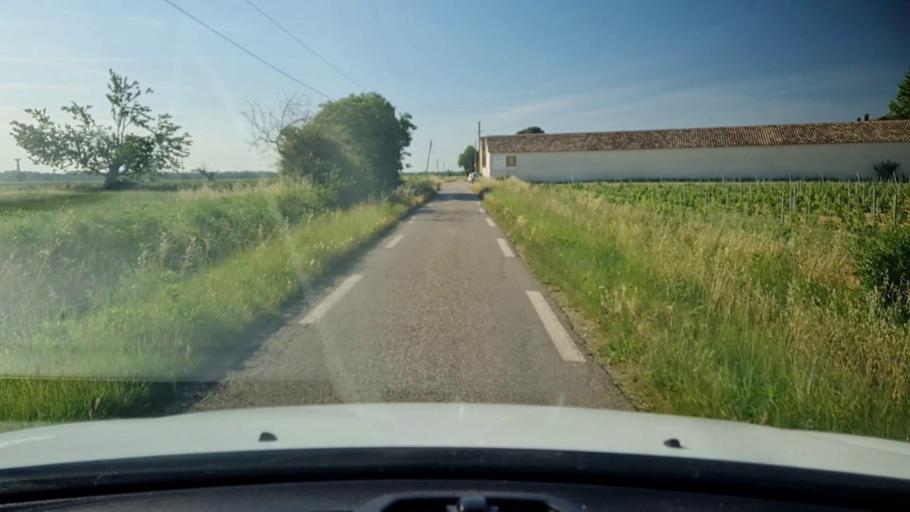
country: FR
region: Languedoc-Roussillon
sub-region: Departement du Gard
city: Le Cailar
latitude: 43.6459
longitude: 4.2232
